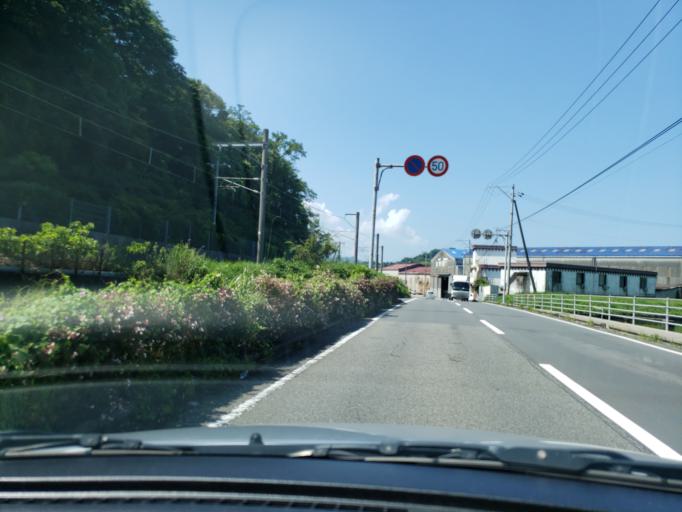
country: JP
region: Ehime
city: Hojo
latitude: 34.0928
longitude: 132.9338
